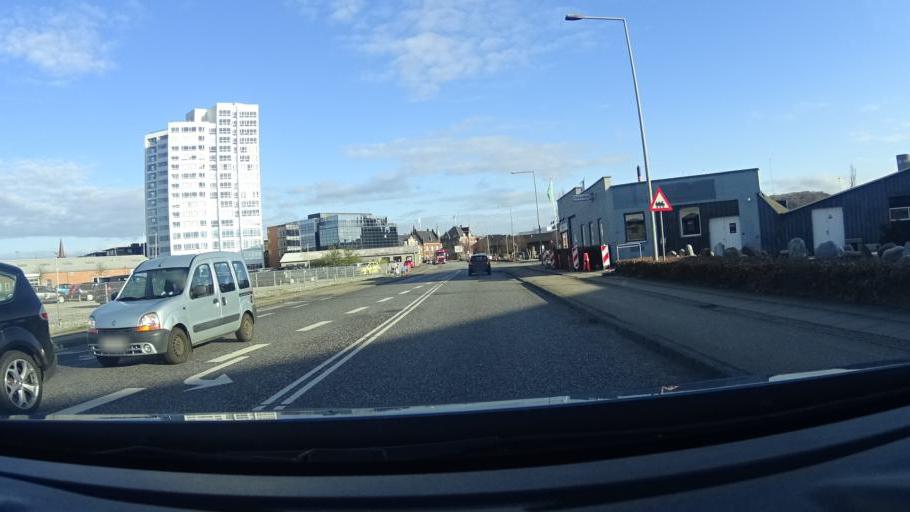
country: DK
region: South Denmark
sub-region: Vejle Kommune
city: Vejle
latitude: 55.7046
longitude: 9.5433
